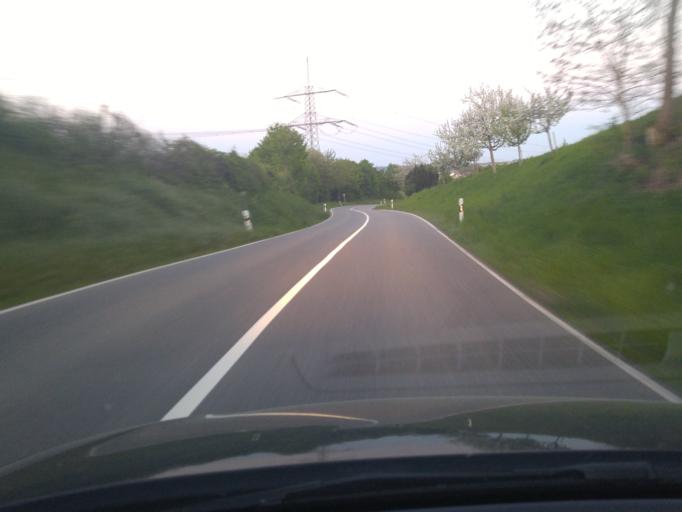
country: DE
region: Baden-Wuerttemberg
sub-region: Regierungsbezirk Stuttgart
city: Bonnigheim
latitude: 49.0423
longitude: 9.0754
